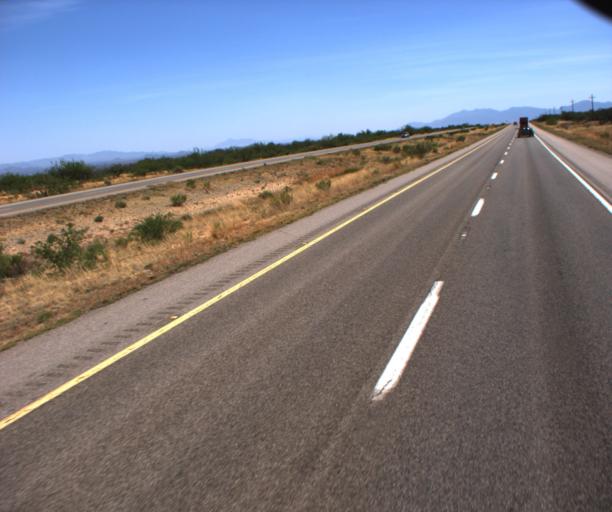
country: US
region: Arizona
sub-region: Cochise County
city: Whetstone
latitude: 31.8653
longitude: -110.3413
